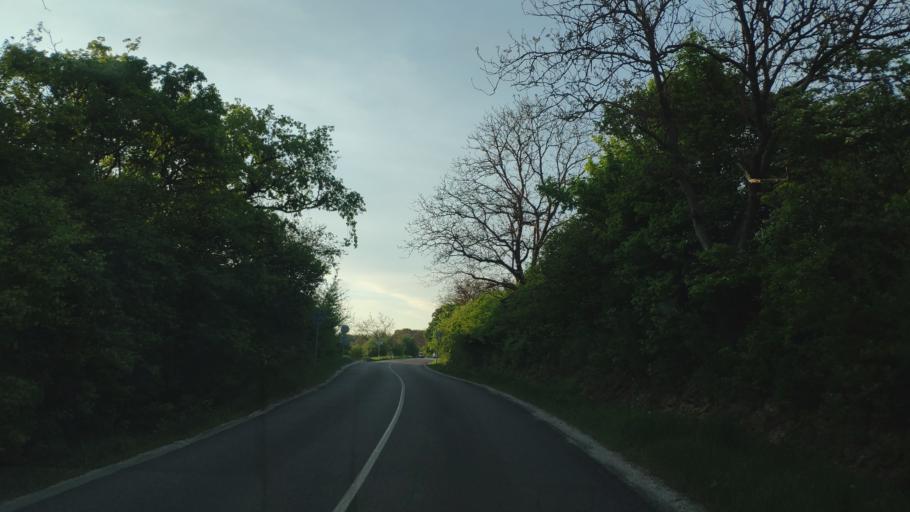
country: SK
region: Kosicky
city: Kosice
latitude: 48.7153
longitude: 21.3067
